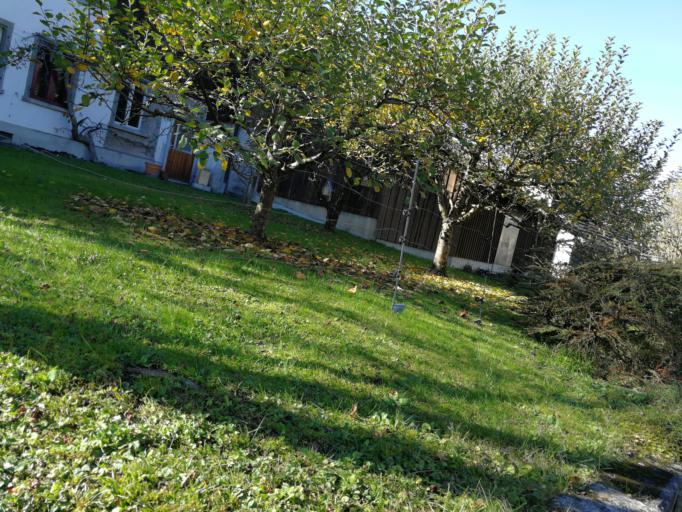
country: CH
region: Zurich
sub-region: Bezirk Meilen
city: Hombrechtikon
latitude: 47.2431
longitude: 8.7766
